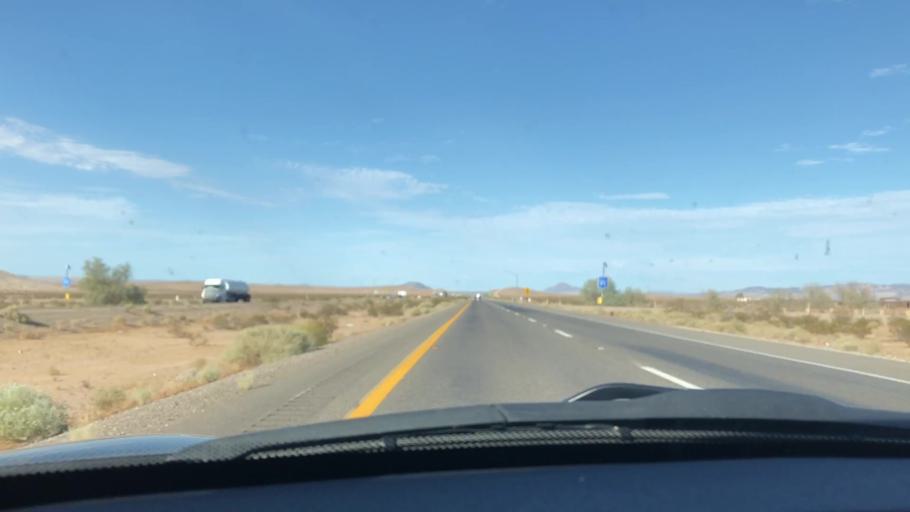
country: US
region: California
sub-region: San Bernardino County
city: Fort Irwin
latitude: 34.9637
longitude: -116.6442
